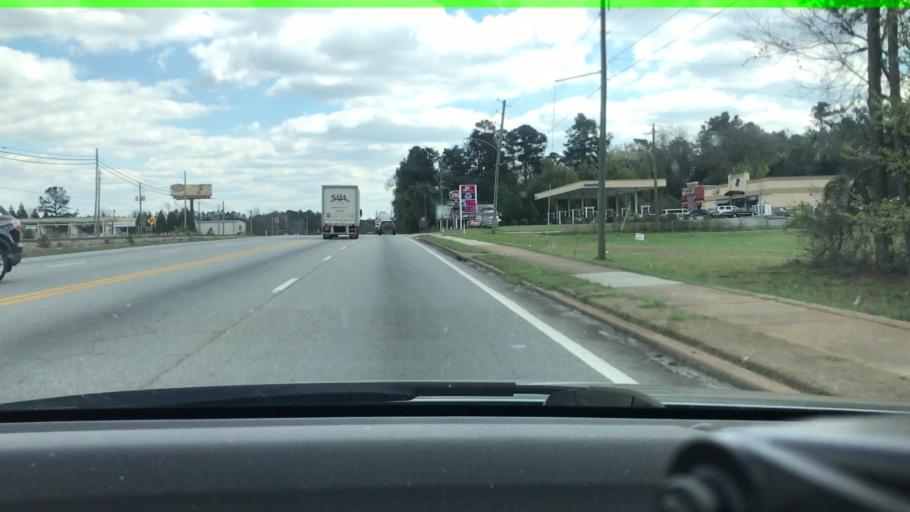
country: US
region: Georgia
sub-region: Clarke County
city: Country Club Estates
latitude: 33.9871
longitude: -83.4215
